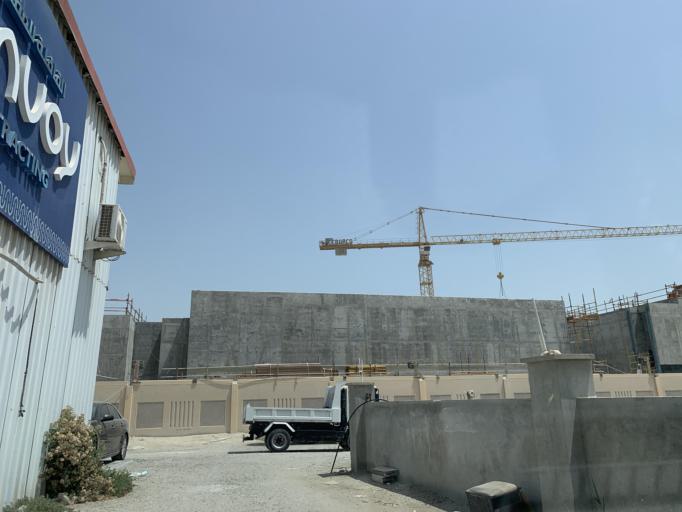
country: BH
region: Northern
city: Madinat `Isa
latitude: 26.1942
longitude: 50.5488
